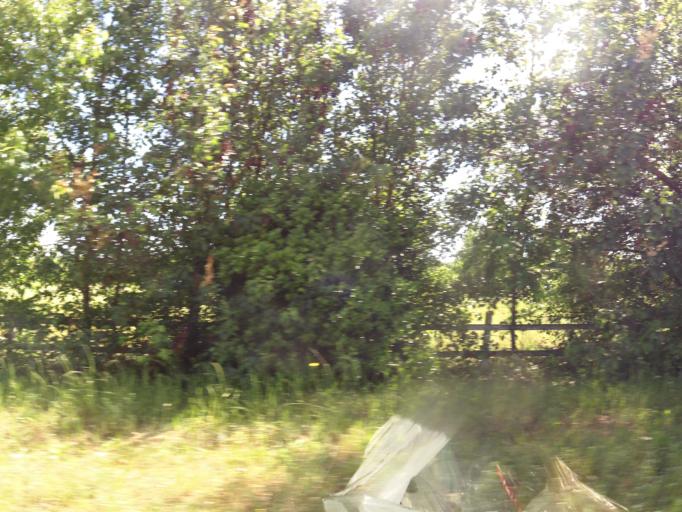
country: US
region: South Carolina
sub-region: Aiken County
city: Aiken
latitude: 33.5517
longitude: -81.6928
